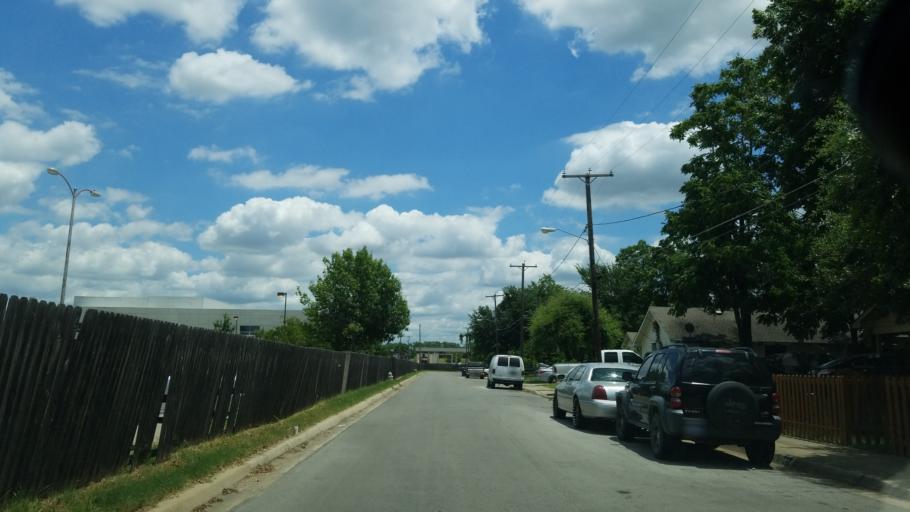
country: US
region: Texas
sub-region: Dallas County
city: Dallas
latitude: 32.7376
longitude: -96.7527
